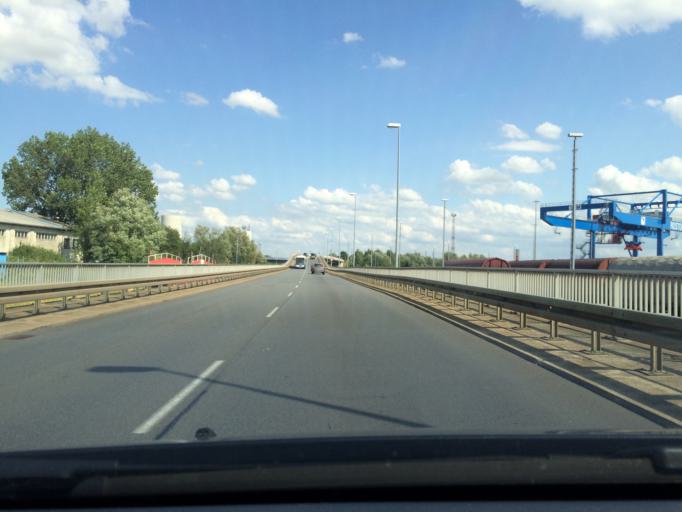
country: DE
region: Mecklenburg-Vorpommern
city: Warnemuende
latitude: 54.1410
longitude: 12.1053
